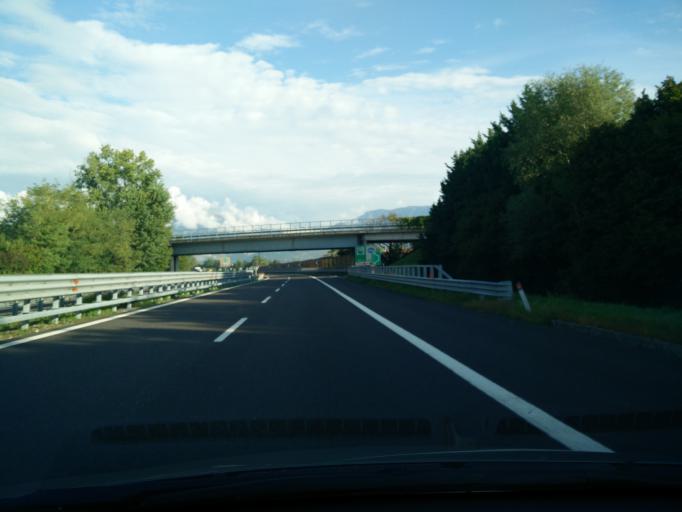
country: IT
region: Veneto
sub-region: Provincia di Treviso
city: Scomigo
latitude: 45.9322
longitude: 12.3132
